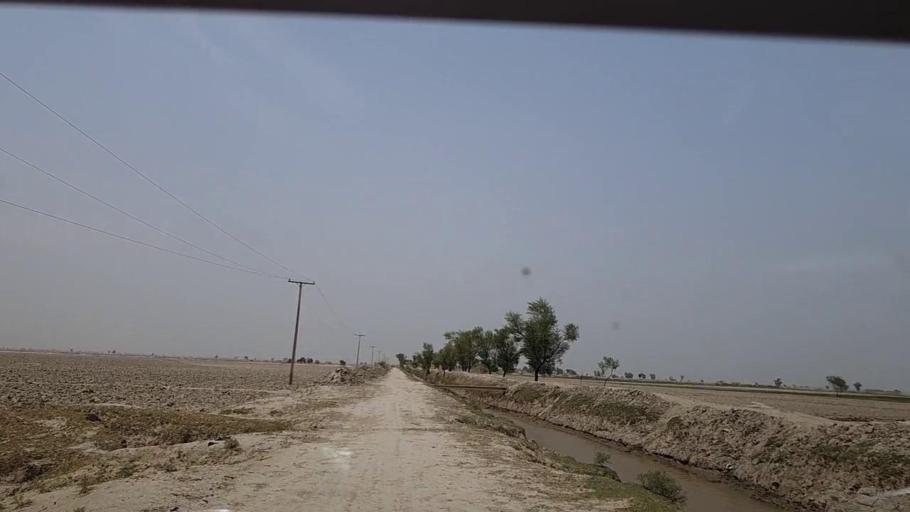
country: PK
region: Sindh
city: Khairpur Nathan Shah
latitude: 27.0480
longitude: 67.6190
